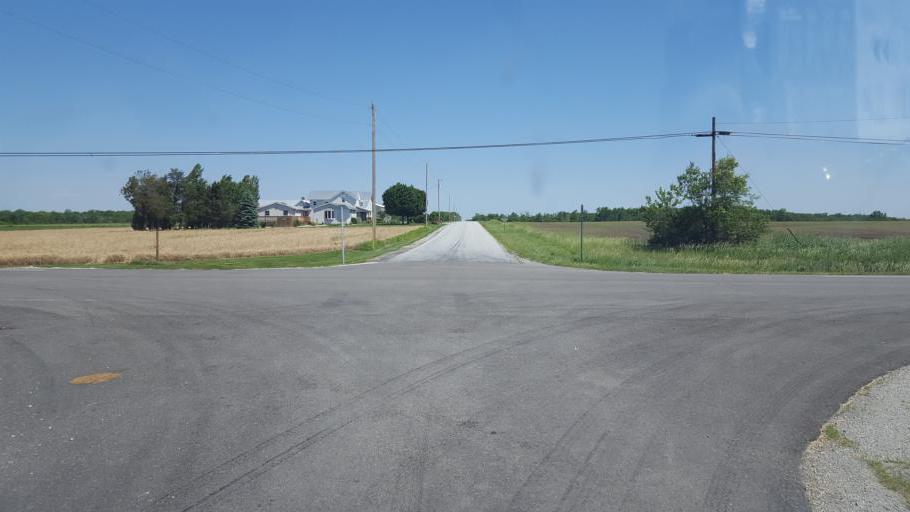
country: US
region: Ohio
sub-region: Hardin County
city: Kenton
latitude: 40.6438
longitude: -83.4389
